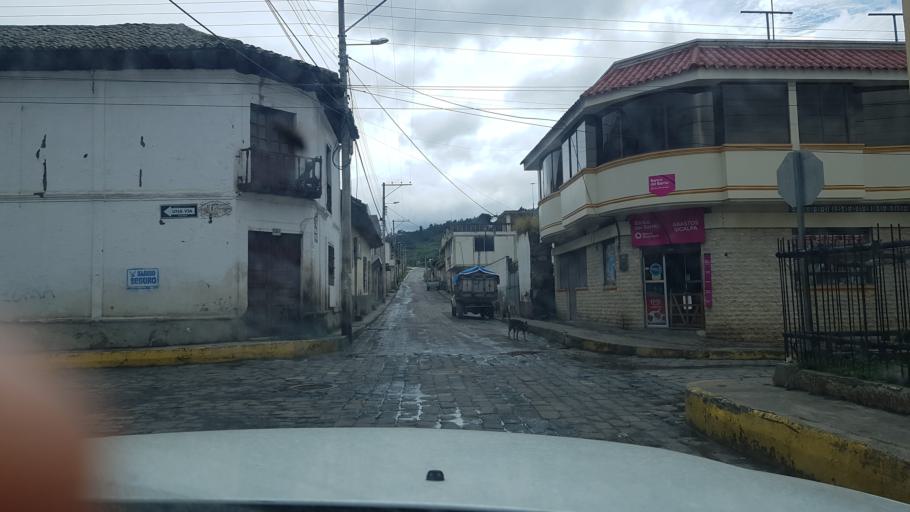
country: EC
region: Chimborazo
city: Riobamba
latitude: -1.7029
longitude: -78.7759
